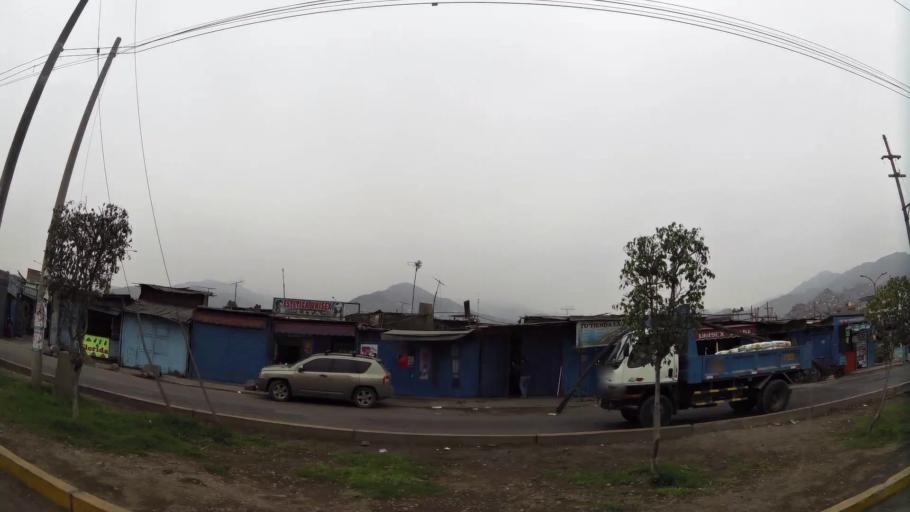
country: PE
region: Lima
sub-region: Lima
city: Independencia
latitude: -11.9605
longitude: -76.9840
